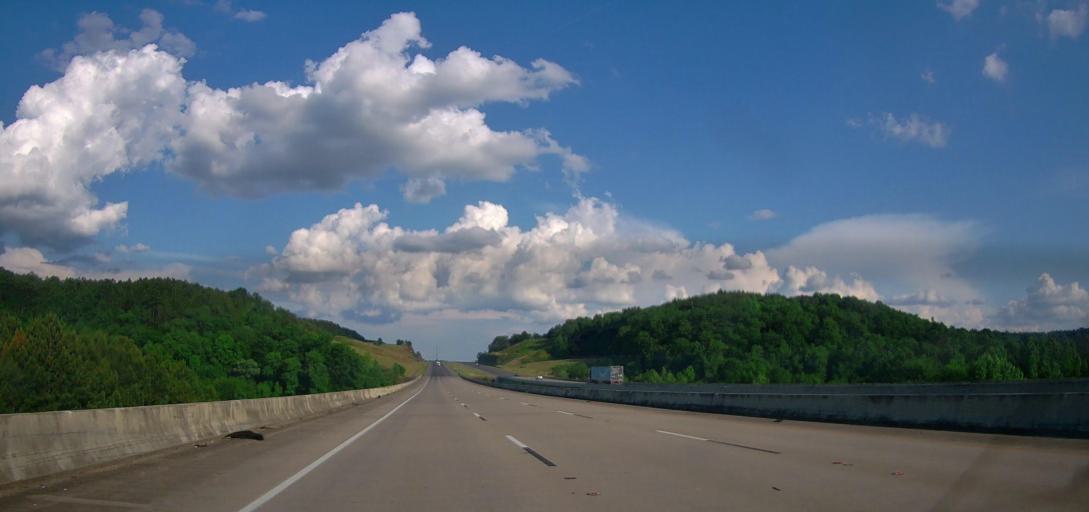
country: US
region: Alabama
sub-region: Walker County
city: Dora
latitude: 33.7086
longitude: -87.1438
